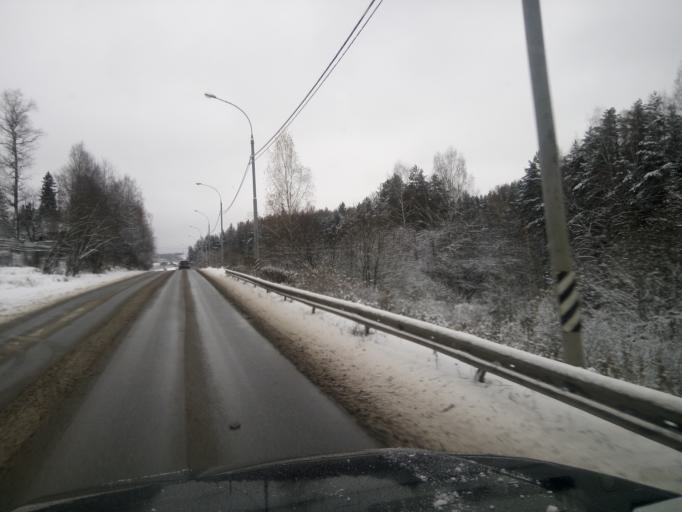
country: RU
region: Moskovskaya
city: Skhodnya
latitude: 55.9650
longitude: 37.3097
